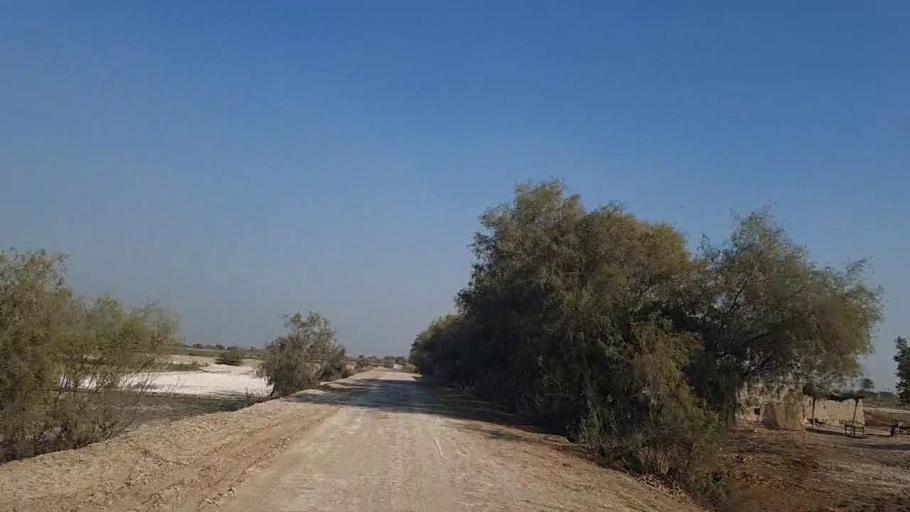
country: PK
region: Sindh
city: Daur
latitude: 26.3177
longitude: 68.1897
